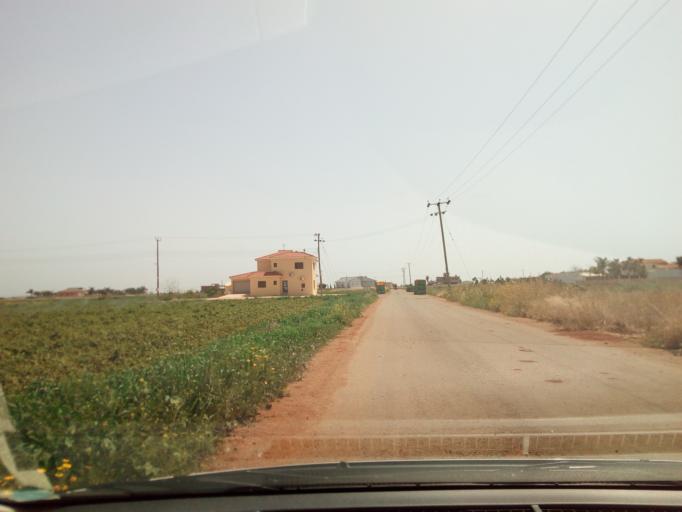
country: CY
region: Ammochostos
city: Avgorou
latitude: 34.9828
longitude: 33.8264
